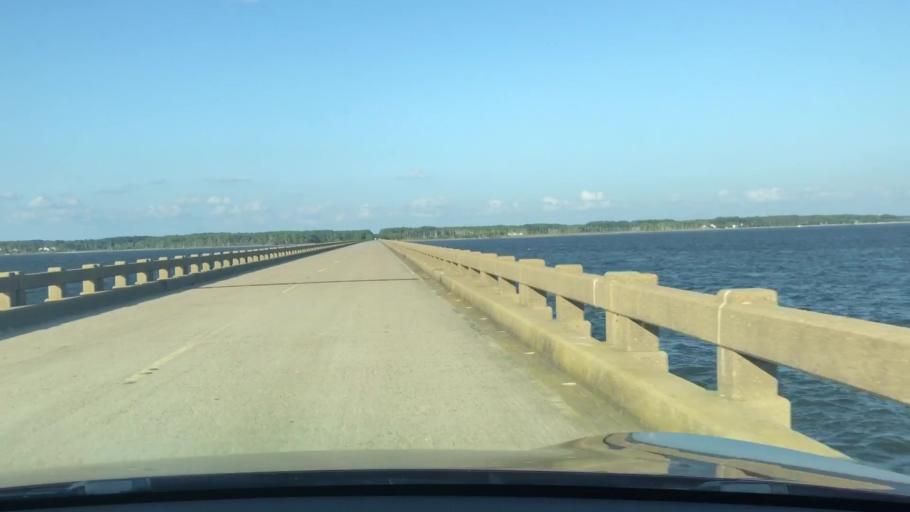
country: US
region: North Carolina
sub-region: Dare County
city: Manteo
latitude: 35.9254
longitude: -75.7370
